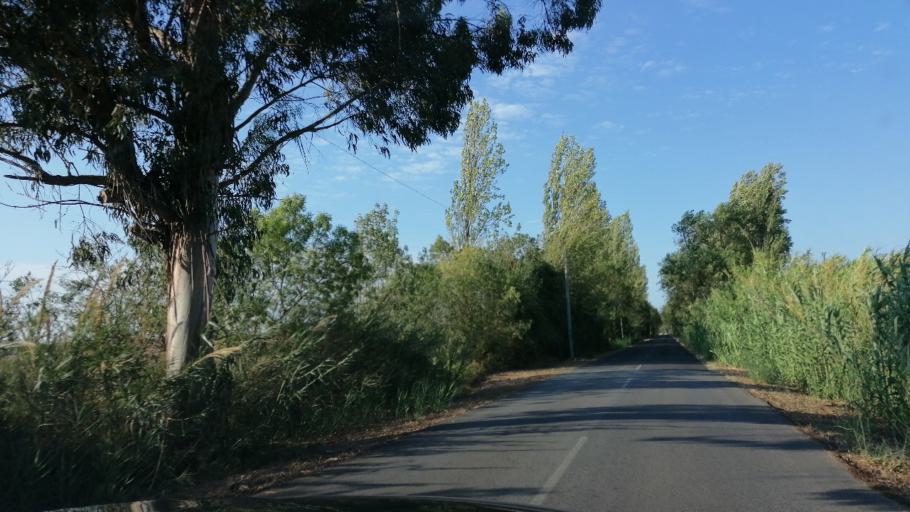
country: PT
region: Santarem
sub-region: Santarem
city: Santarem
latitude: 39.2653
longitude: -8.6645
